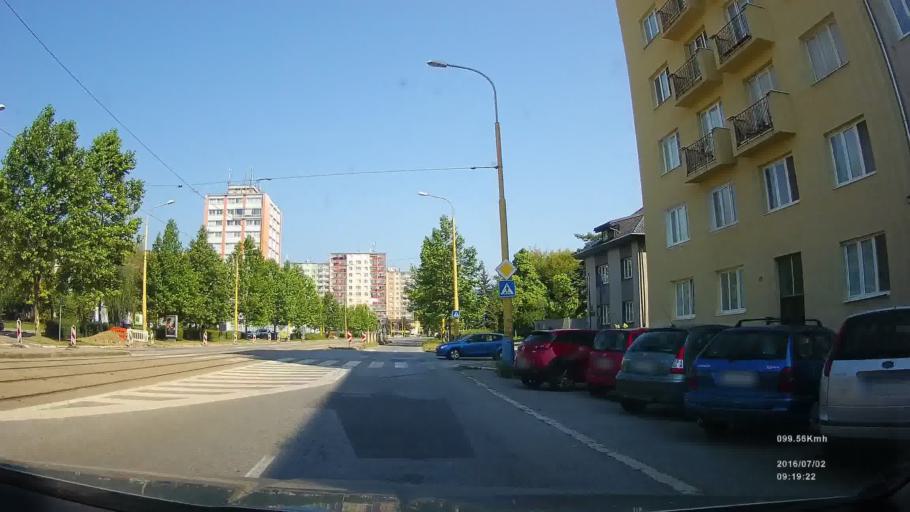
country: SK
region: Kosicky
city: Kosice
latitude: 48.7369
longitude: 21.2338
